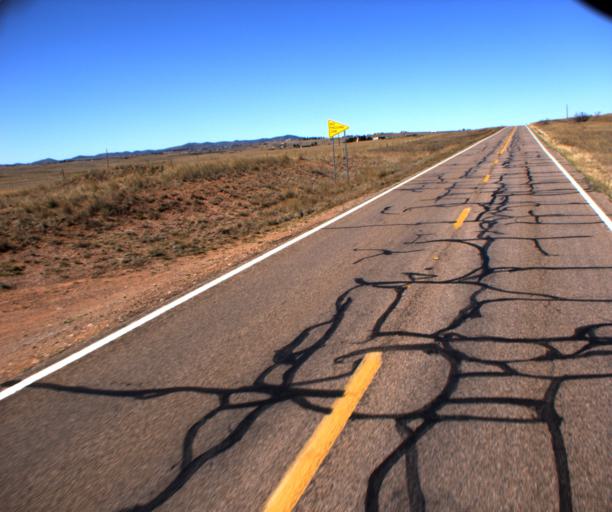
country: US
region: Arizona
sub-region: Cochise County
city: Huachuca City
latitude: 31.6944
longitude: -110.6038
